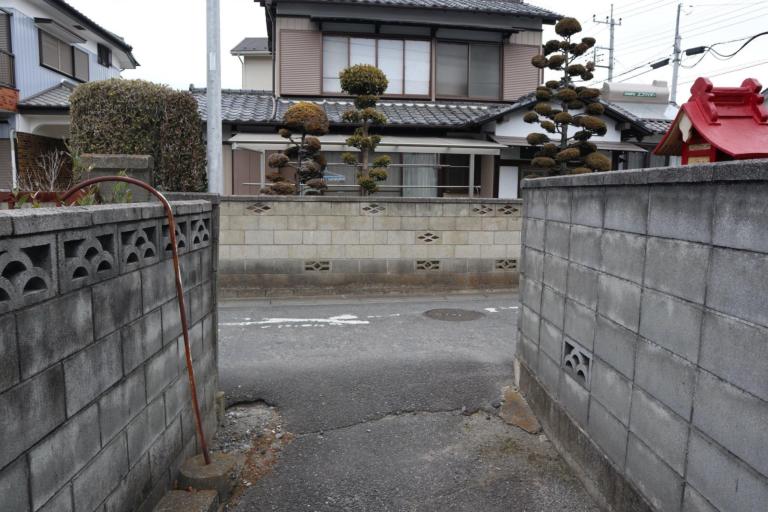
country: JP
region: Saitama
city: Fukiage-fujimi
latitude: 36.1091
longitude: 139.4494
